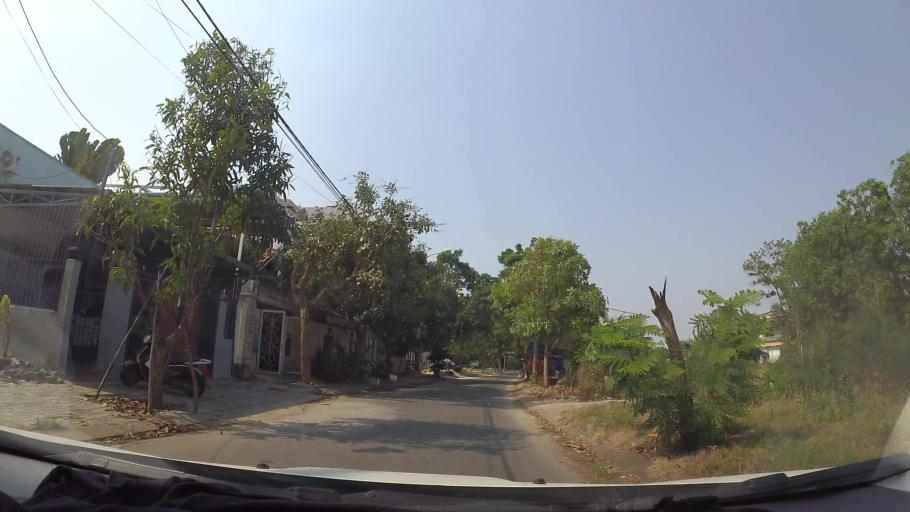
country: VN
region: Da Nang
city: Cam Le
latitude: 16.0096
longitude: 108.1978
